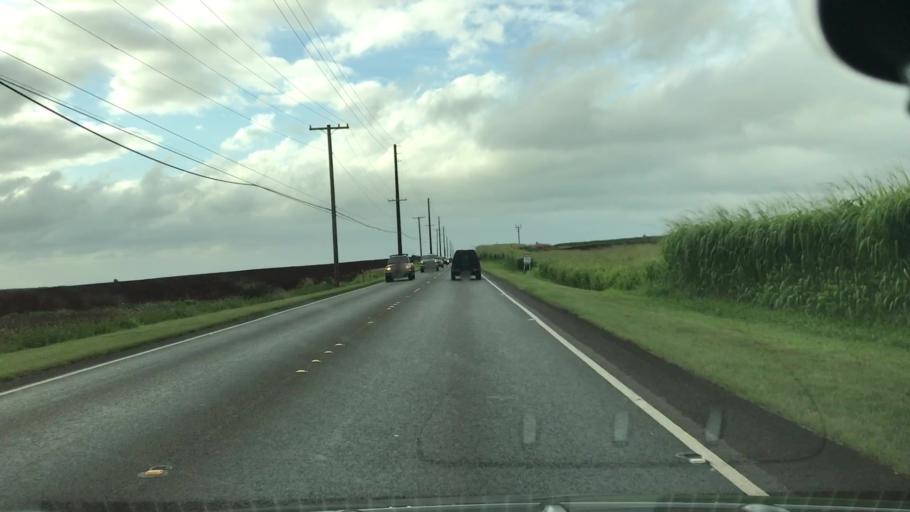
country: US
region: Hawaii
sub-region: Honolulu County
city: Whitmore Village
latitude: 21.5326
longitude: -158.0410
